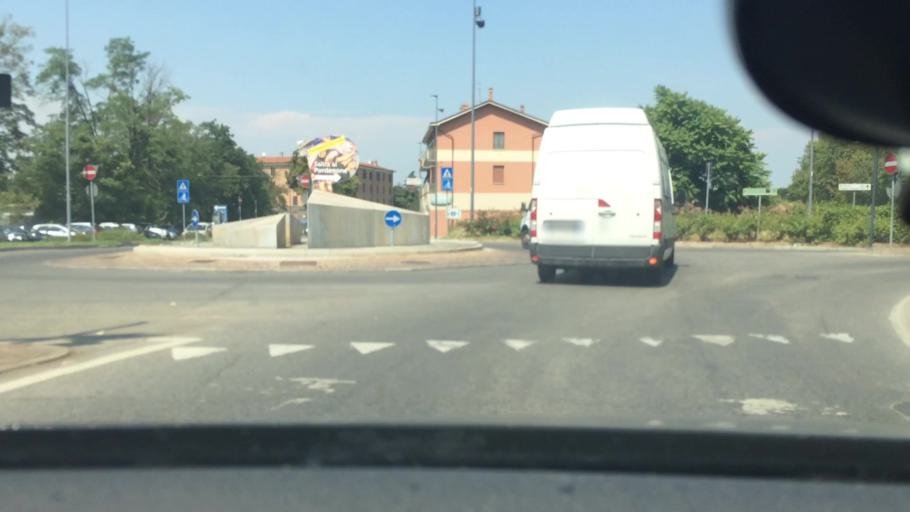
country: IT
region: Emilia-Romagna
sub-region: Provincia di Piacenza
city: Piacenza
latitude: 45.0566
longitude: 9.6781
